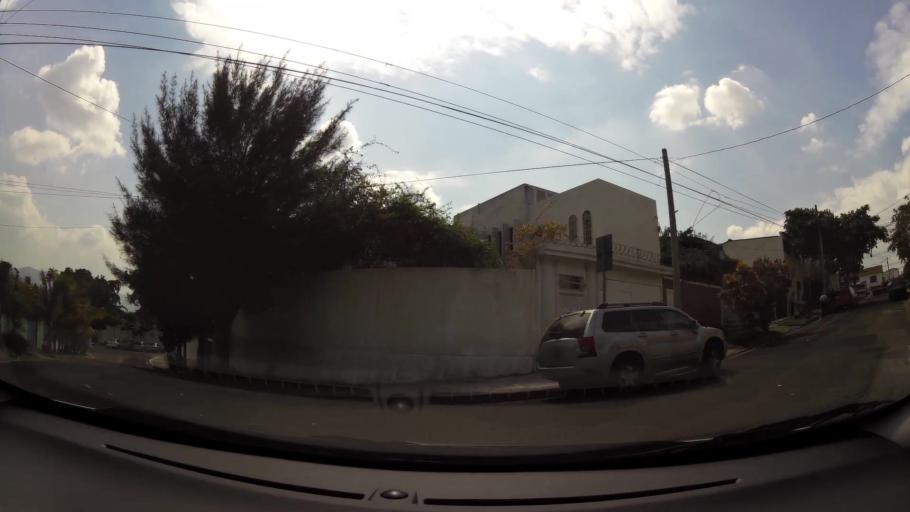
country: SV
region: San Salvador
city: Mejicanos
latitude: 13.7061
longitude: -89.2207
